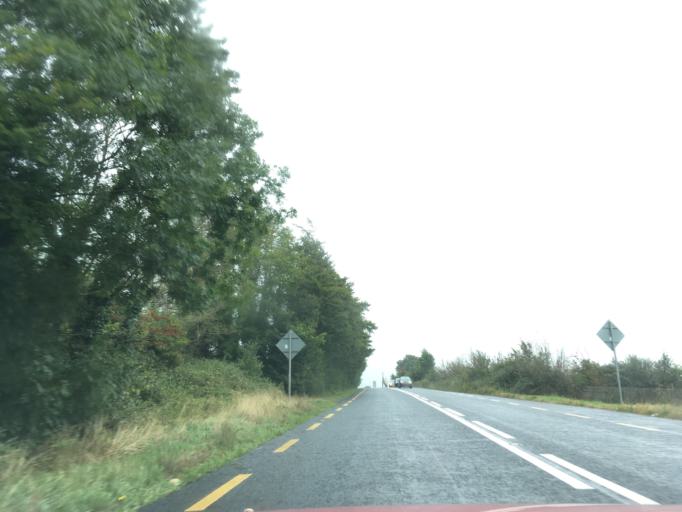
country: IE
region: Munster
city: Carrick-on-Suir
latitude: 52.3521
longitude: -7.4679
